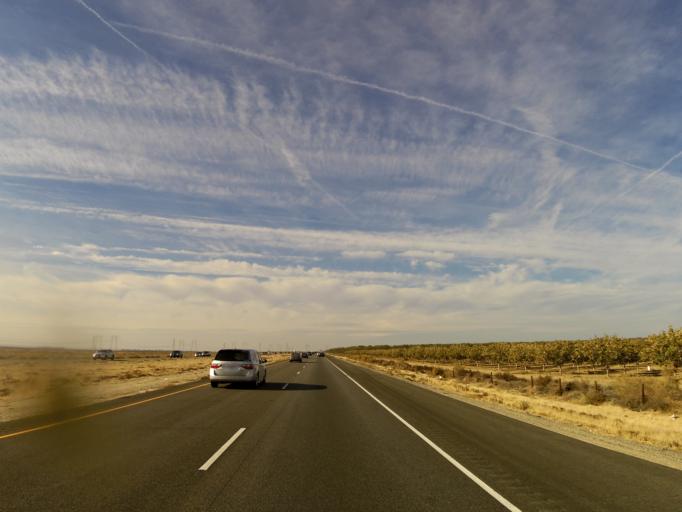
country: US
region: California
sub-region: Kern County
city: Buttonwillow
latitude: 35.4761
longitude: -119.5030
